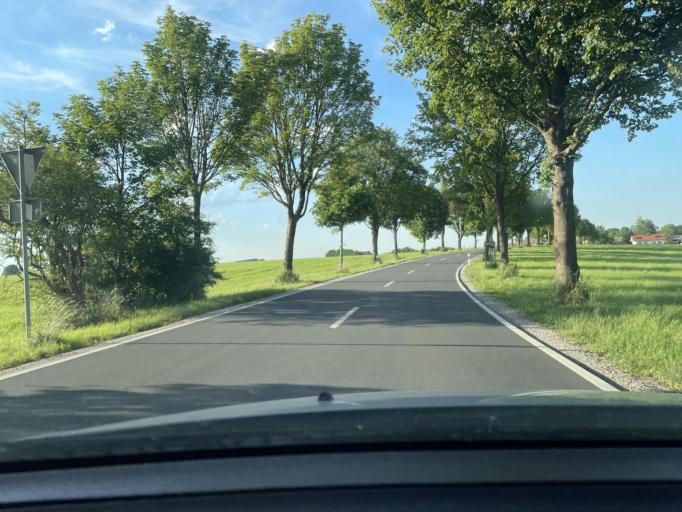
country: DE
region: Bavaria
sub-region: Upper Bavaria
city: Holzkirchen
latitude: 47.8900
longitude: 11.7088
